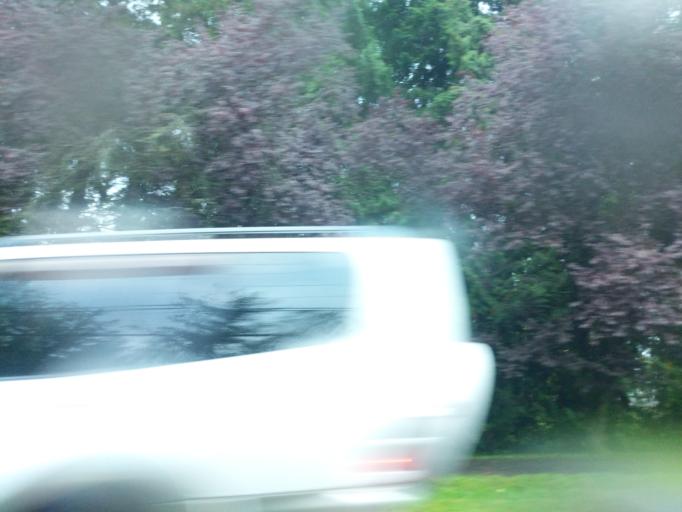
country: US
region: Washington
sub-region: King County
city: Bothell
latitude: 47.7794
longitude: -122.2072
